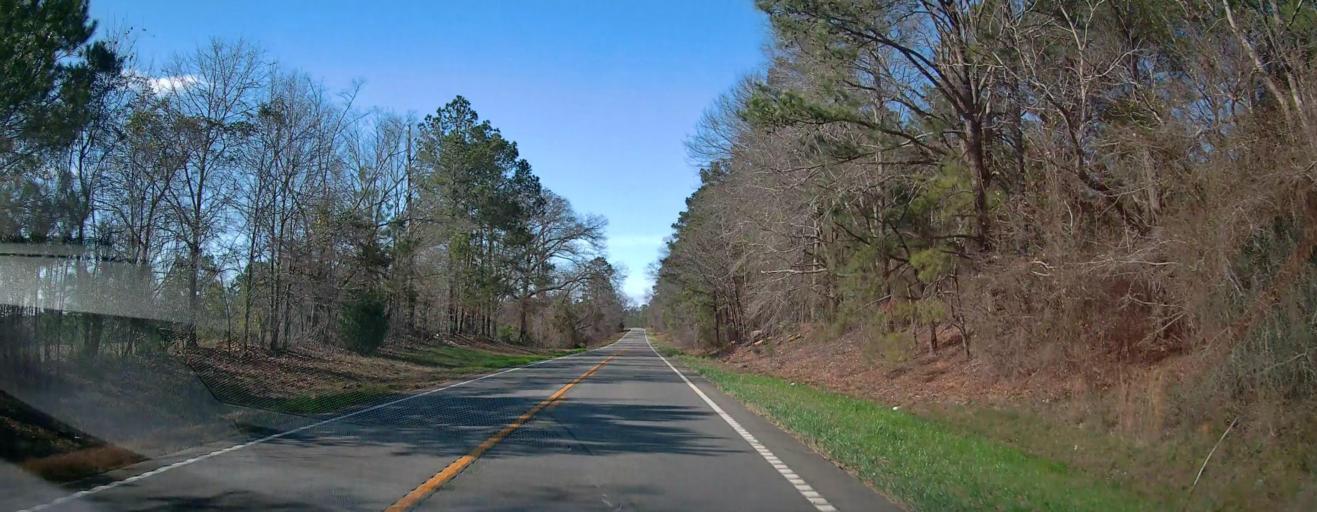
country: US
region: Georgia
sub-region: Macon County
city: Oglethorpe
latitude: 32.3398
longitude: -84.1306
